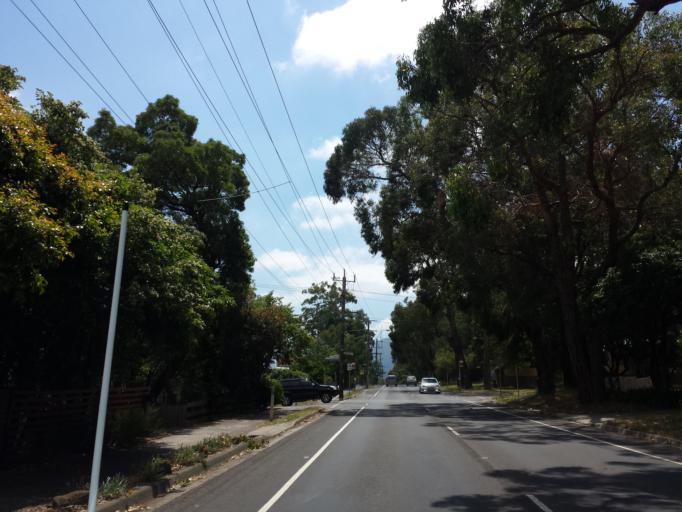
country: AU
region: Victoria
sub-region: Knox
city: The Basin
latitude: -37.8596
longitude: 145.3110
